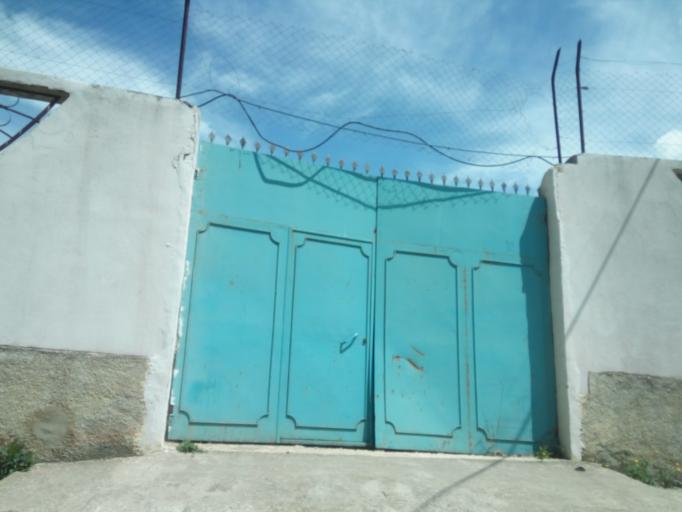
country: DZ
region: Constantine
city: Constantine
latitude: 36.3751
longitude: 6.6166
